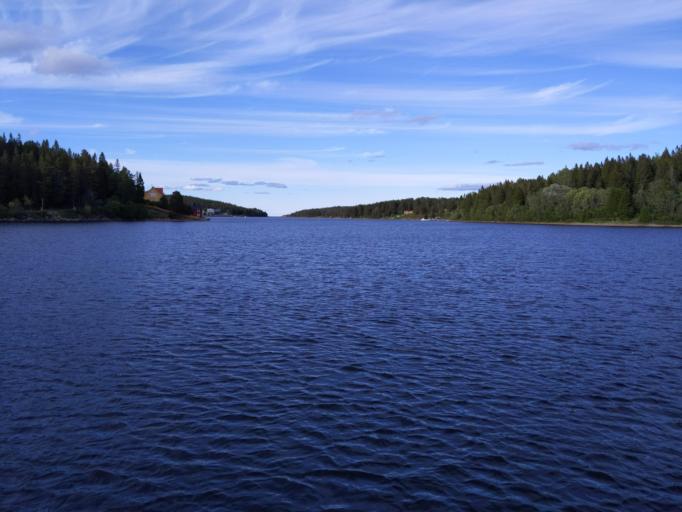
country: SE
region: Vaesternorrland
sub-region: OErnskoeldsviks Kommun
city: Kopmanholmen
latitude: 63.0153
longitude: 18.6382
